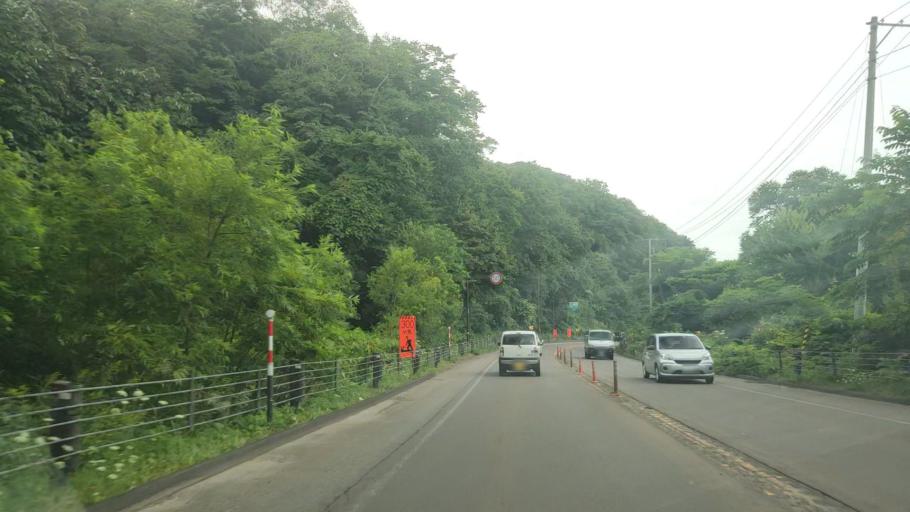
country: JP
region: Hokkaido
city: Nanae
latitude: 41.9727
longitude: 140.6487
